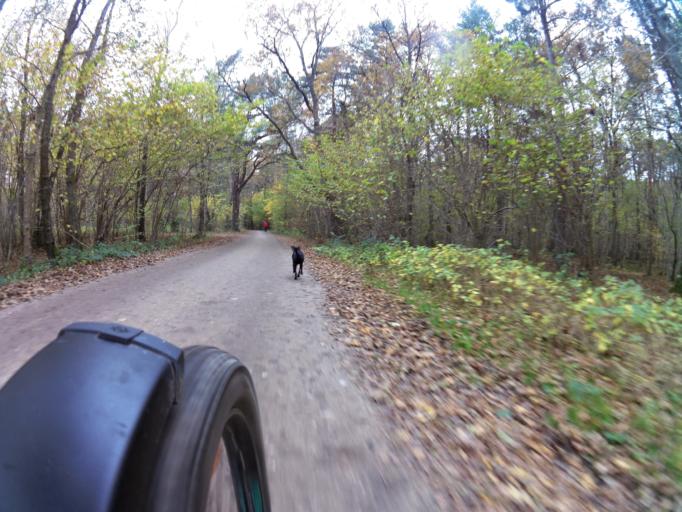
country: PL
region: Pomeranian Voivodeship
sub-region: Powiat pucki
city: Krokowa
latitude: 54.8288
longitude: 18.0991
